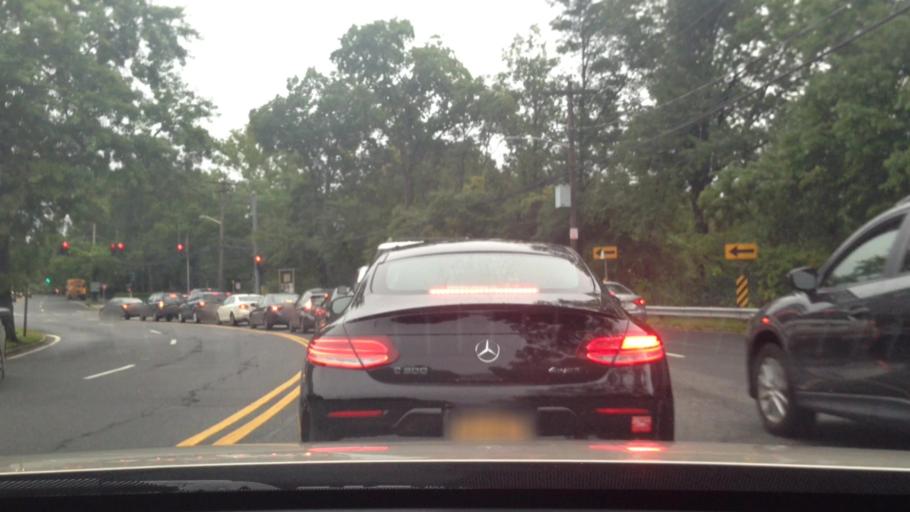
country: US
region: New York
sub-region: Nassau County
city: Thomaston
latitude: 40.7872
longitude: -73.7054
